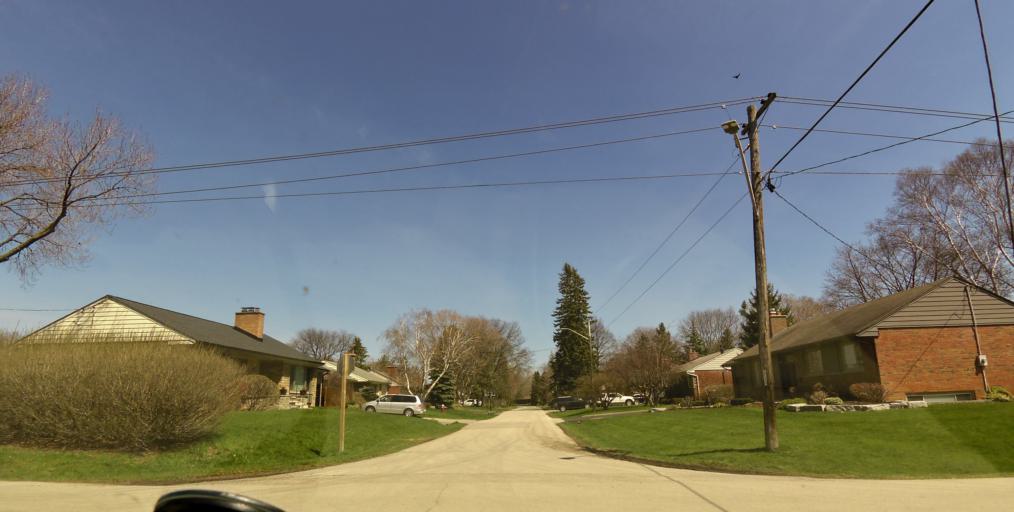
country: CA
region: Ontario
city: Etobicoke
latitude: 43.6005
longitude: -79.5608
